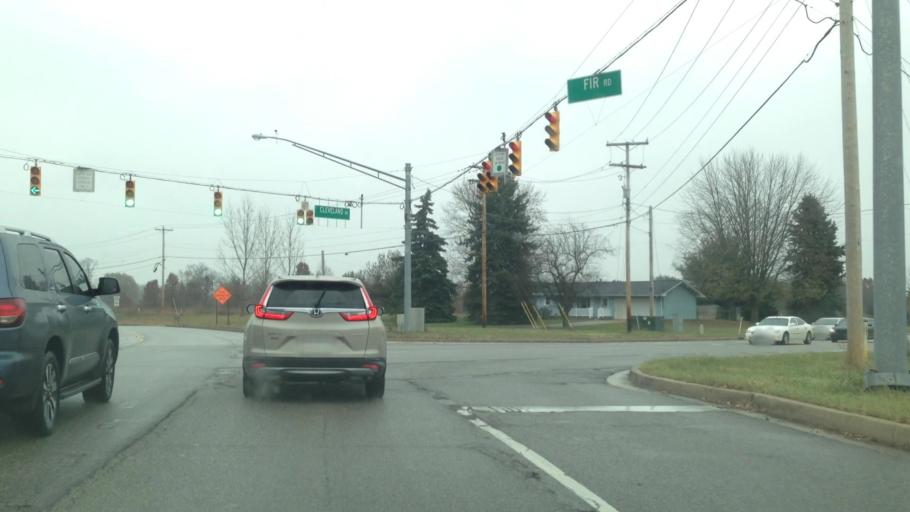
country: US
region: Indiana
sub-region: Saint Joseph County
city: Granger
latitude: 41.7241
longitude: -86.1594
